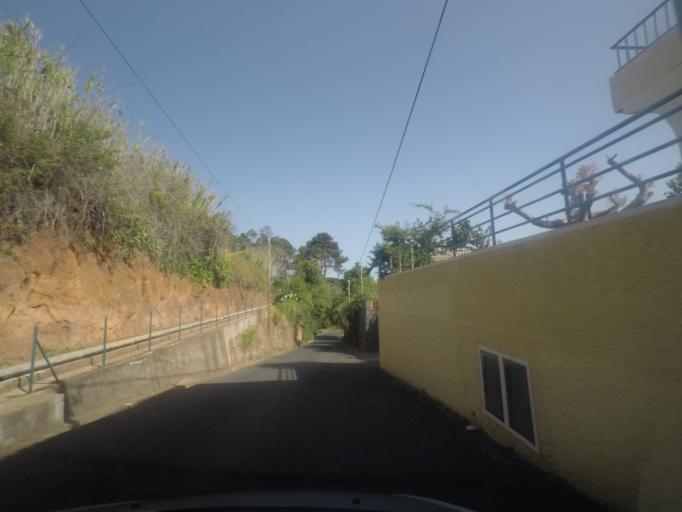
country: PT
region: Madeira
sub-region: Calheta
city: Estreito da Calheta
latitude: 32.7591
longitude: -17.2017
